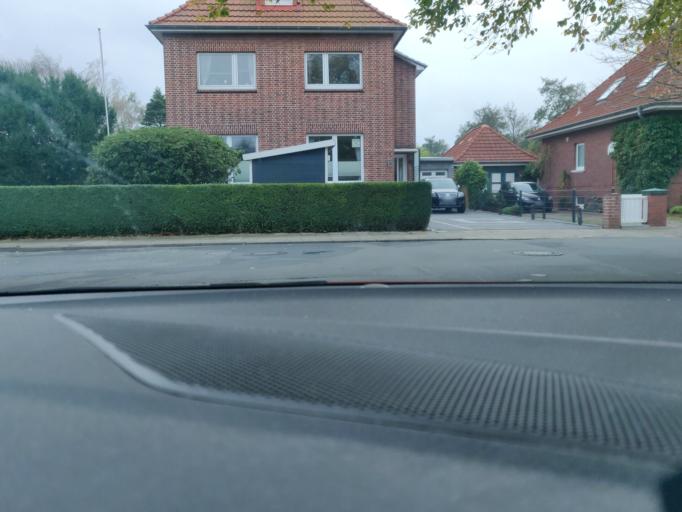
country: DE
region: Lower Saxony
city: Cuxhaven
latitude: 53.8842
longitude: 8.6767
